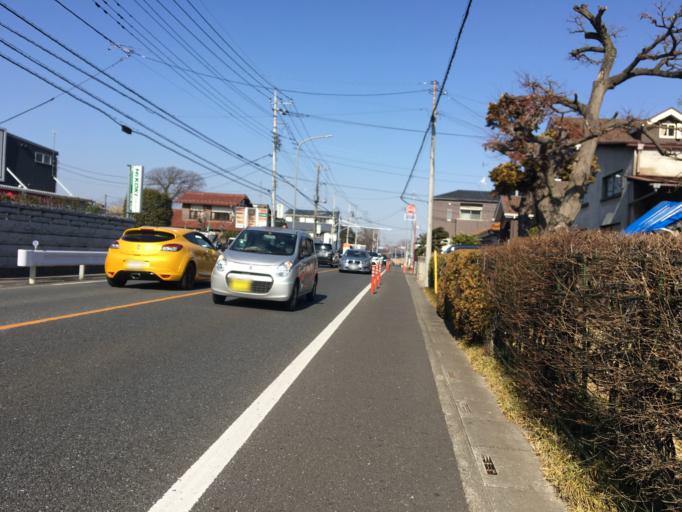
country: JP
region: Saitama
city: Oi
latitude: 35.8464
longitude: 139.5198
